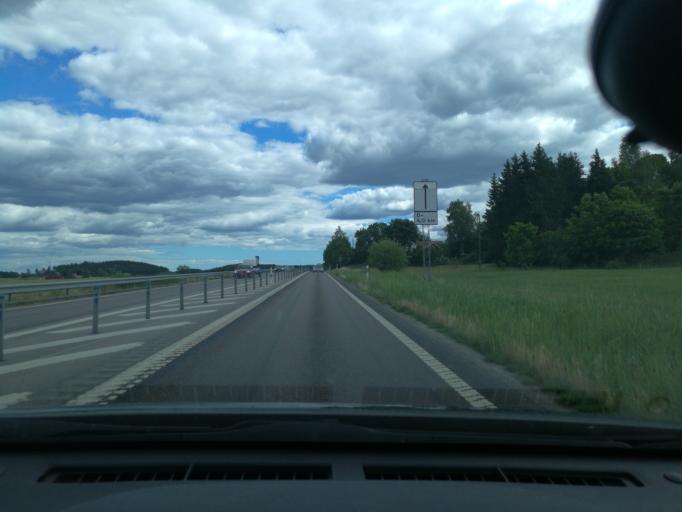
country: SE
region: OEstergoetland
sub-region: Soderkopings Kommun
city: Soederkoeping
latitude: 58.5413
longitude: 16.2726
